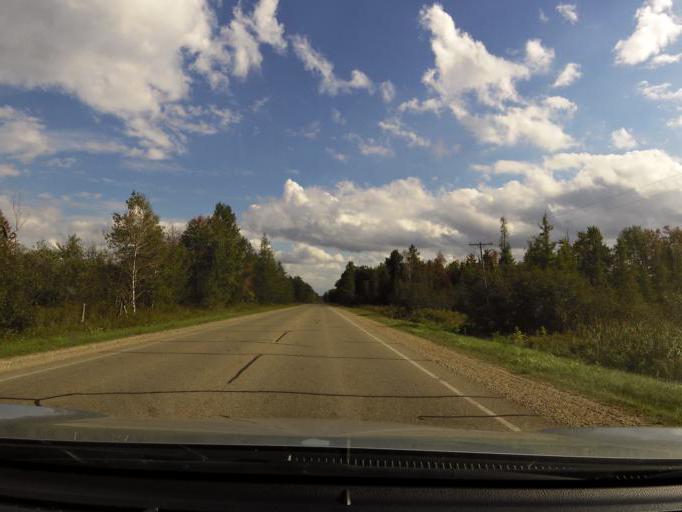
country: US
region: Michigan
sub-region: Roscommon County
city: Saint Helen
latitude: 44.3926
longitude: -84.4343
